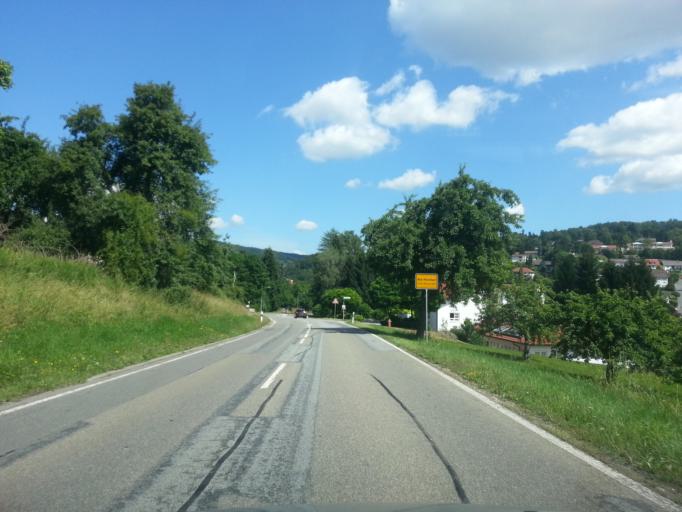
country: DE
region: Hesse
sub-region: Regierungsbezirk Darmstadt
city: Wald-Michelbach
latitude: 49.5713
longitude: 8.8209
